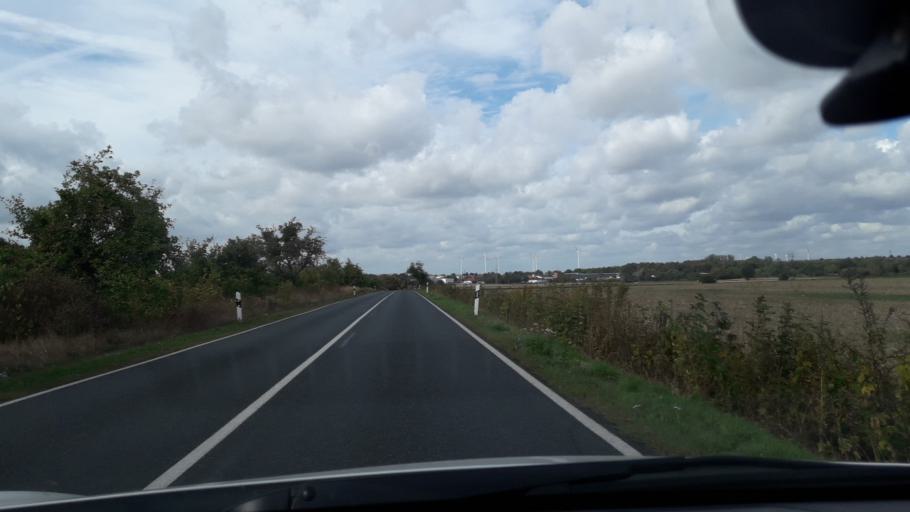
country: DE
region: Lower Saxony
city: Alt Wallmoden
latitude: 52.0292
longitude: 10.3370
